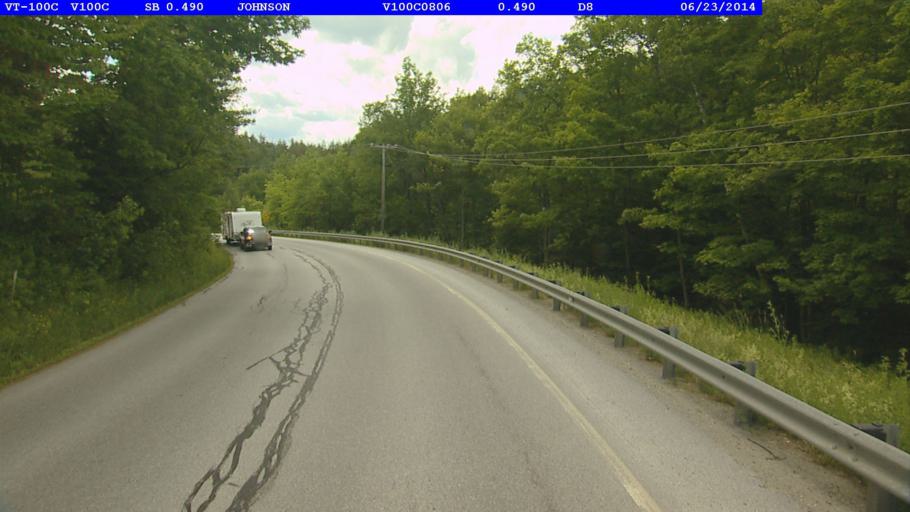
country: US
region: Vermont
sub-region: Lamoille County
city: Johnson
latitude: 44.6377
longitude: -72.6695
